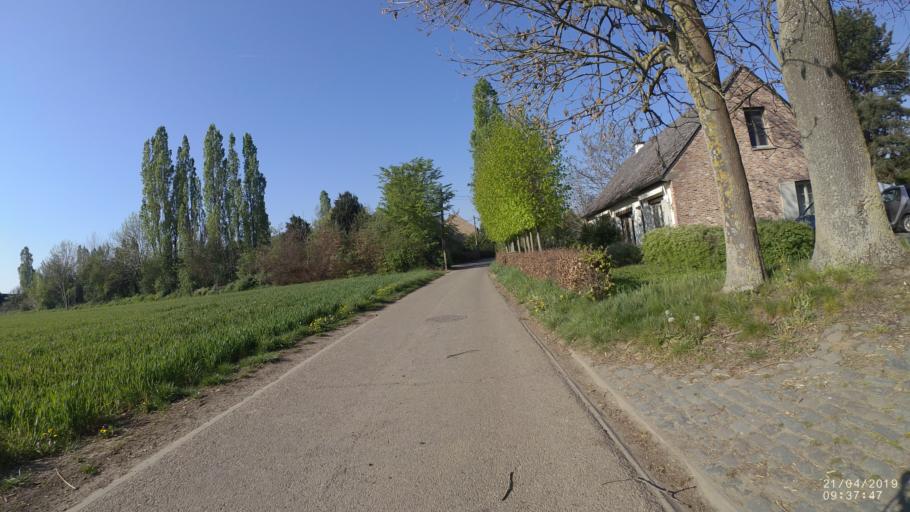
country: BE
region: Flanders
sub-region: Provincie Vlaams-Brabant
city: Lubbeek
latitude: 50.9195
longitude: 4.8310
